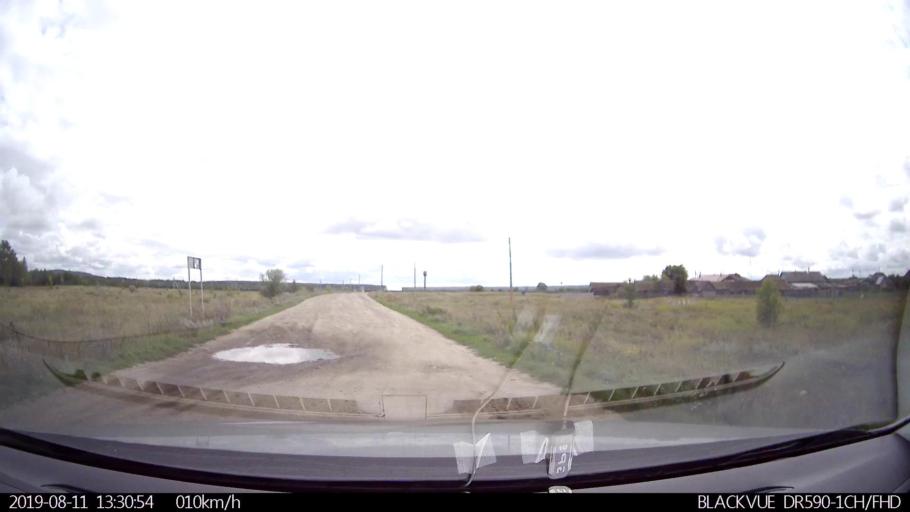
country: RU
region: Ulyanovsk
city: Ignatovka
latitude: 53.8602
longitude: 47.5997
